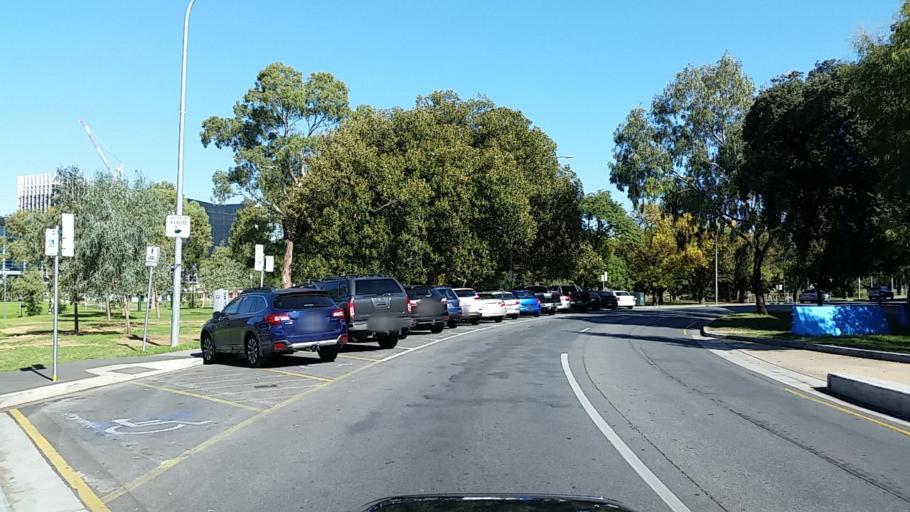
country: AU
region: South Australia
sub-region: Adelaide
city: Adelaide
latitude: -34.9179
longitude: 138.5963
